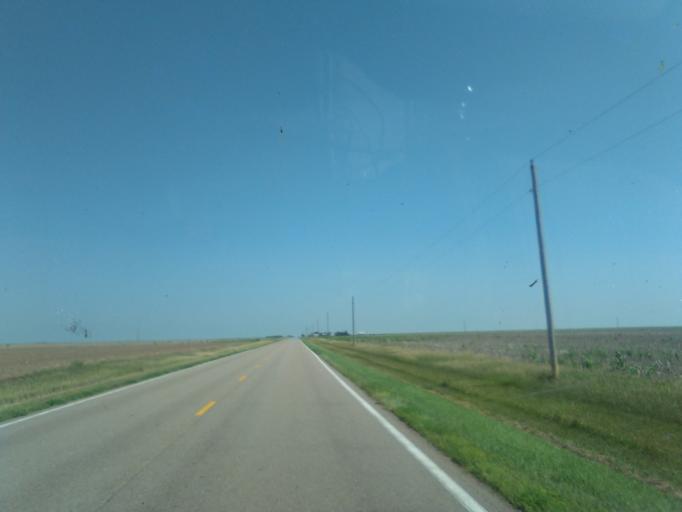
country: US
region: Nebraska
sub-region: Dundy County
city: Benkelman
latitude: 39.8048
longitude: -101.5417
